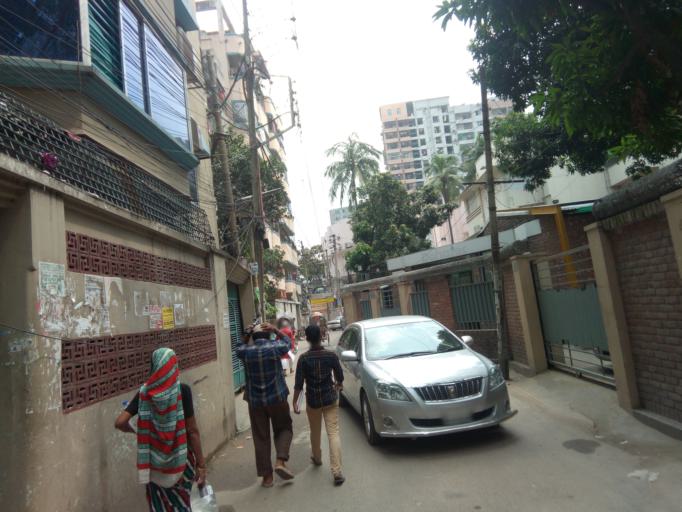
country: BD
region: Dhaka
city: Paltan
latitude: 23.7347
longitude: 90.4124
